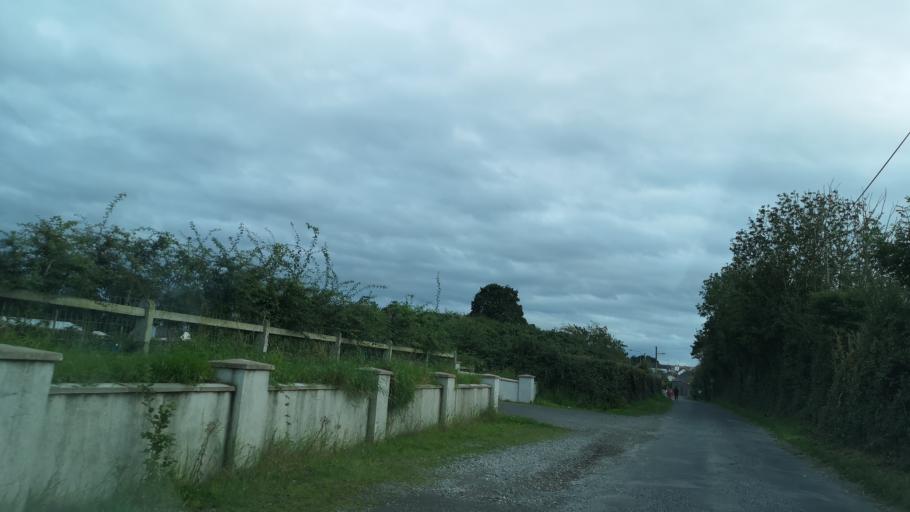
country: IE
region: Leinster
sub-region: Uibh Fhaili
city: Ferbane
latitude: 53.1793
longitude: -7.7268
